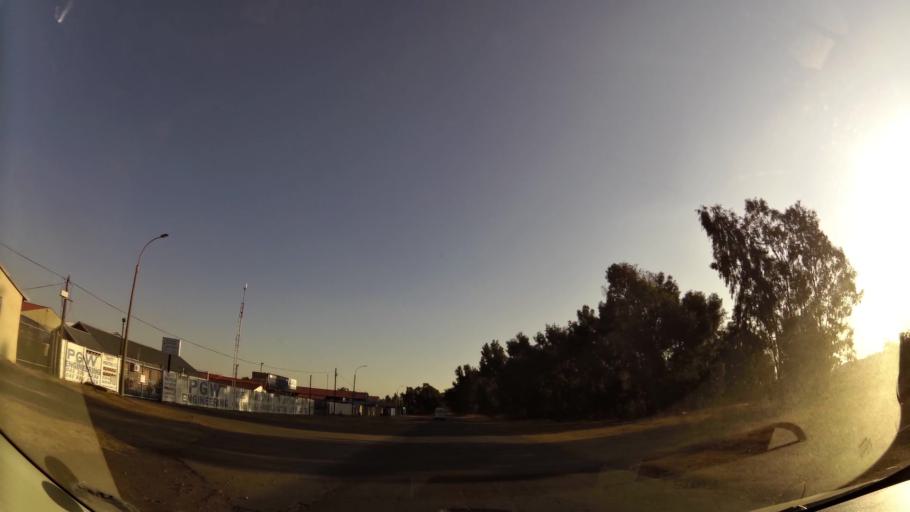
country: ZA
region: Gauteng
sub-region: West Rand District Municipality
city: Randfontein
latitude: -26.1939
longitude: 27.6823
